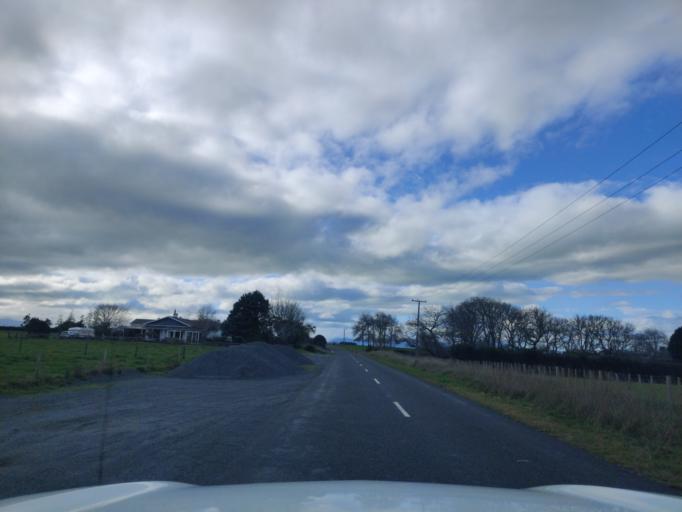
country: NZ
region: Waikato
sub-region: Hauraki District
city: Paeroa
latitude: -37.5895
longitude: 175.5057
